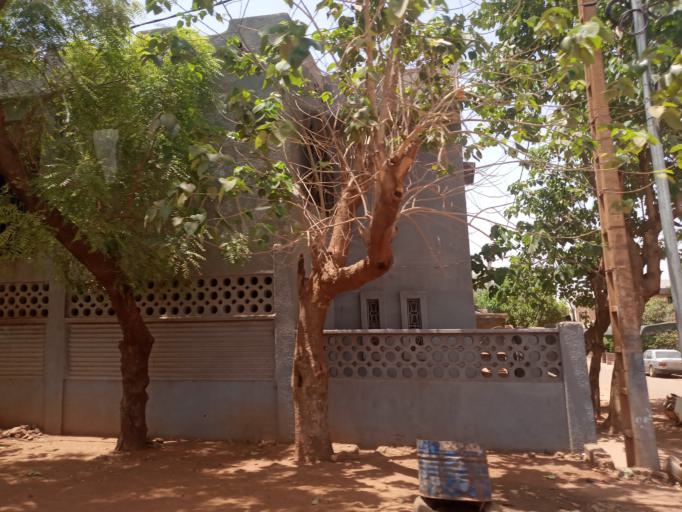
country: ML
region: Bamako
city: Bamako
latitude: 12.6159
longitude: -7.9981
